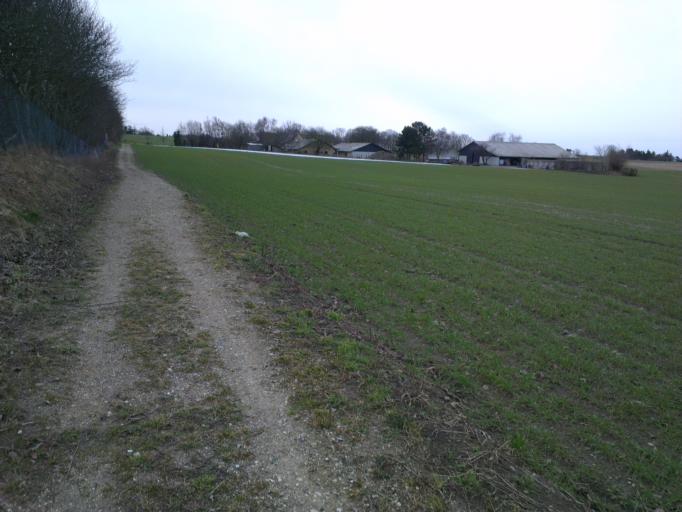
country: DK
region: Zealand
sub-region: Lejre Kommune
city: Ejby
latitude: 55.7609
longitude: 11.8743
